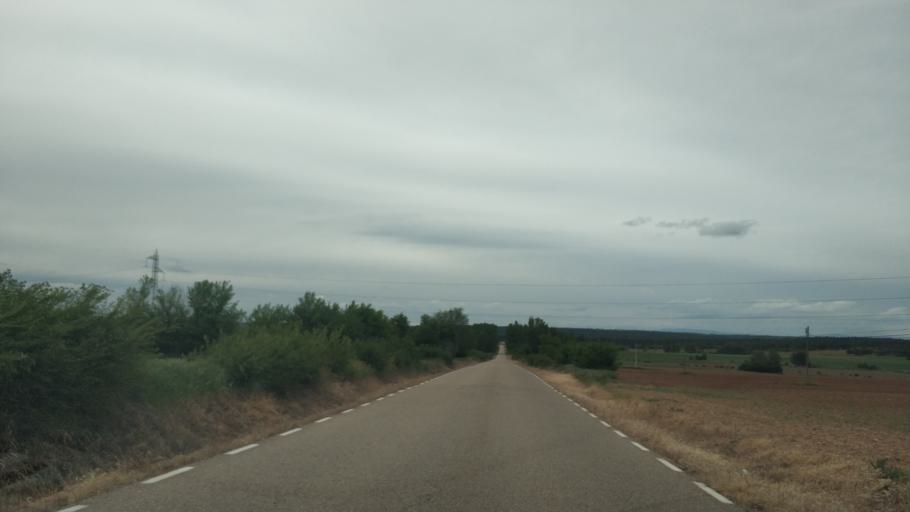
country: ES
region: Castille and Leon
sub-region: Provincia de Soria
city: Berlanga de Duero
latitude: 41.4843
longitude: -2.8654
